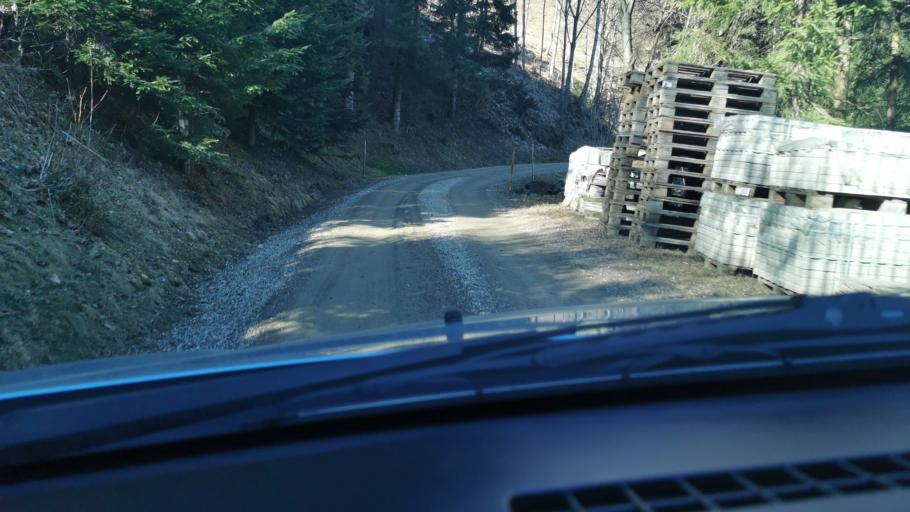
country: AT
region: Styria
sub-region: Politischer Bezirk Weiz
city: Birkfeld
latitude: 47.3588
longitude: 15.6459
